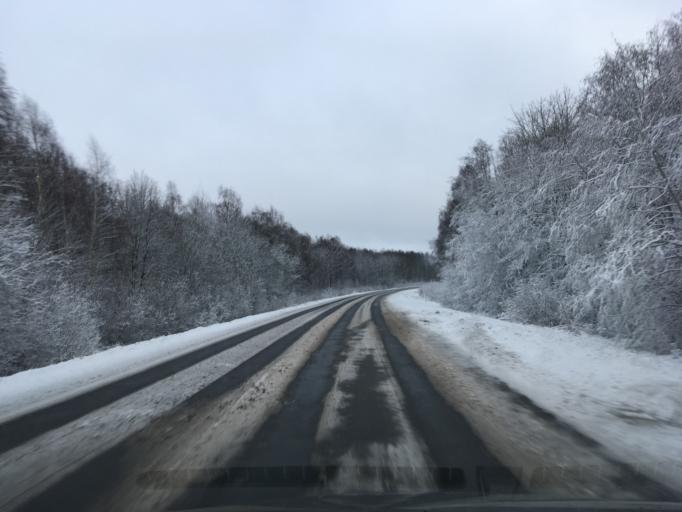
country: EE
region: Harju
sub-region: Raasiku vald
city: Arukula
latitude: 59.3442
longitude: 25.1241
